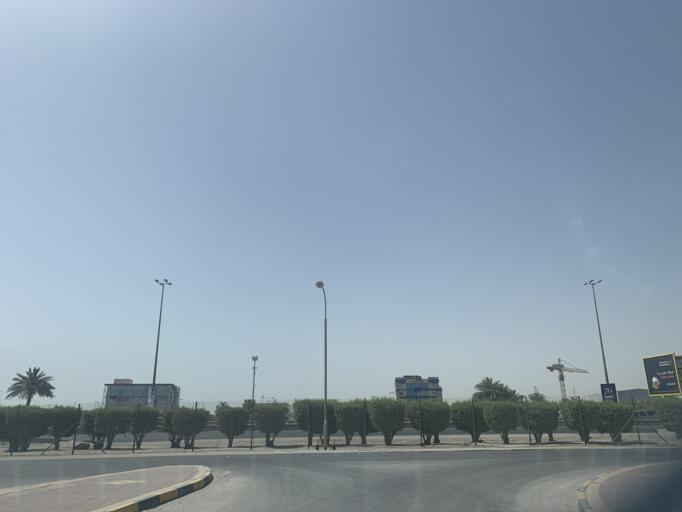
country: BH
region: Manama
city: Jidd Hafs
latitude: 26.1994
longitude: 50.5556
